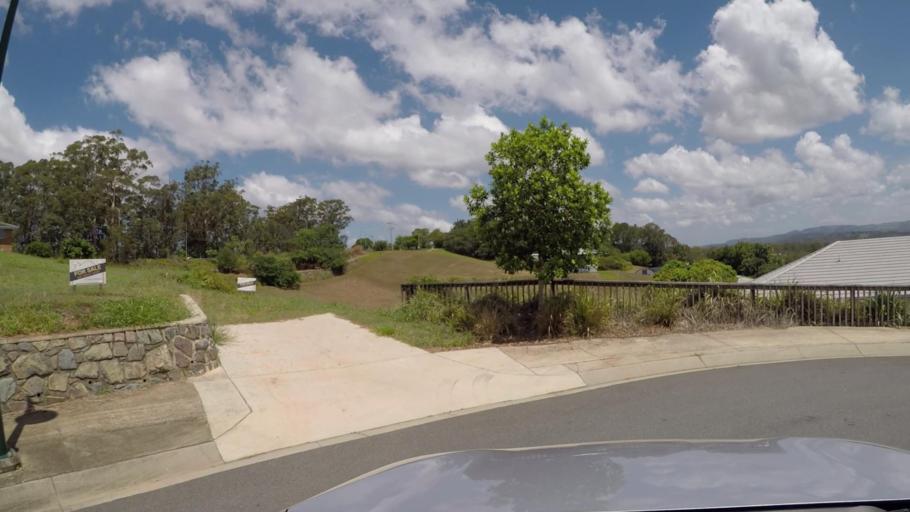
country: AU
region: Queensland
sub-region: Sunshine Coast
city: Woombye
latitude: -26.6709
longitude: 152.9730
